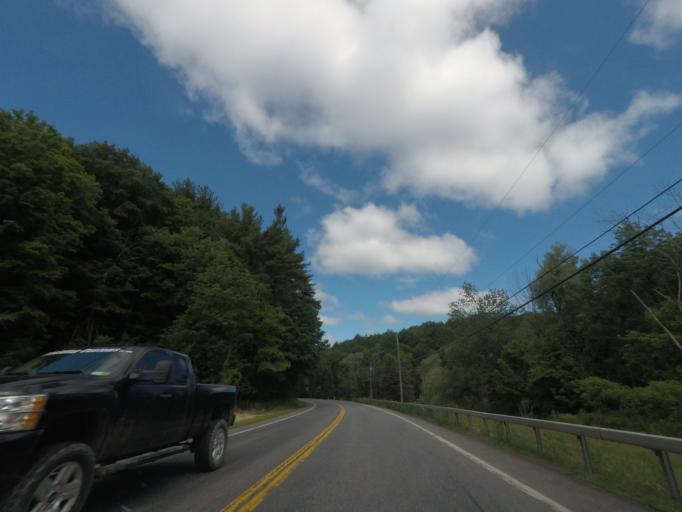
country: US
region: New York
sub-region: Columbia County
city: Philmont
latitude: 42.2069
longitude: -73.6701
